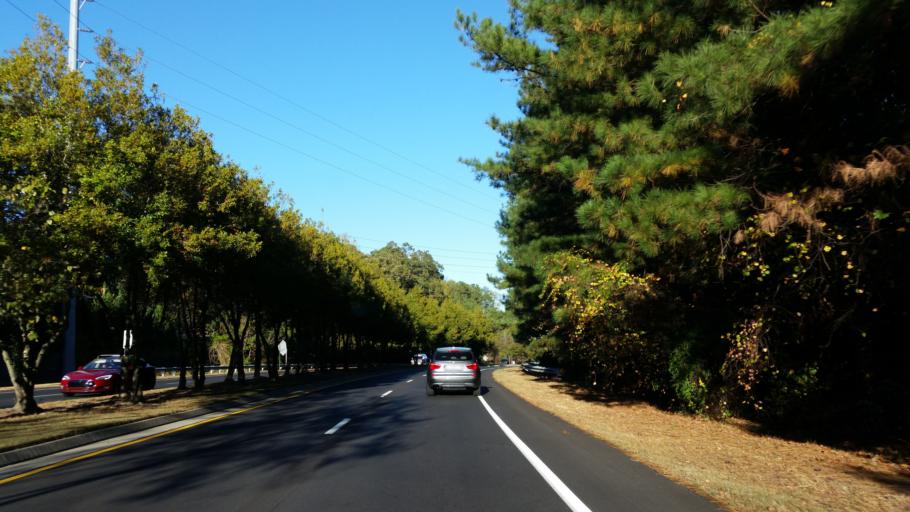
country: US
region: Georgia
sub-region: Fulton County
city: Roswell
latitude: 34.0081
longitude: -84.3856
